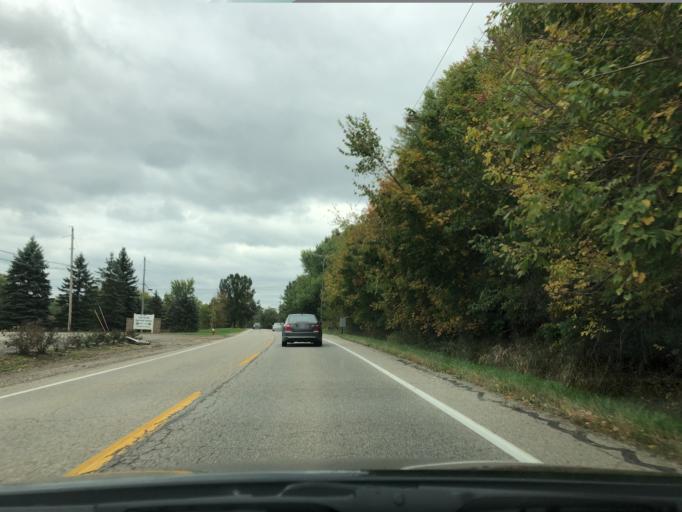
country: US
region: Ohio
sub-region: Summit County
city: Cuyahoga Falls
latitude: 41.1742
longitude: -81.4944
